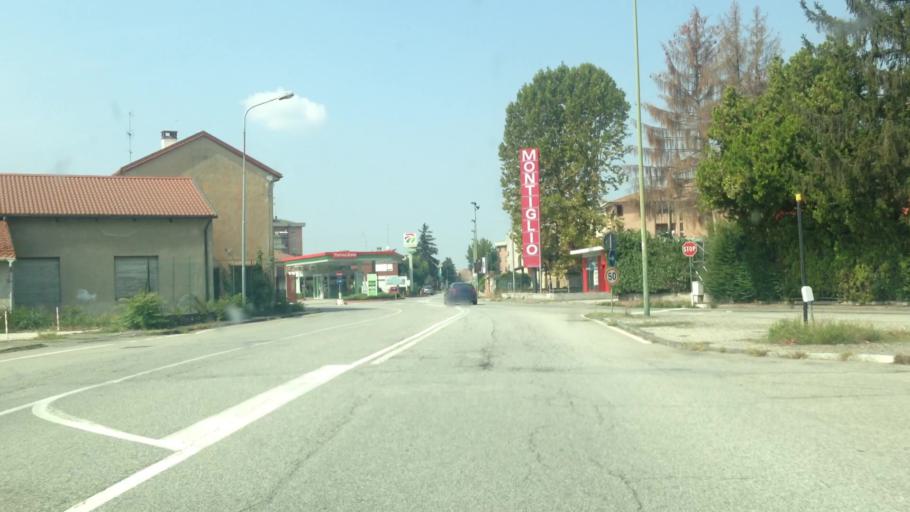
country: IT
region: Piedmont
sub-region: Provincia di Alessandria
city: Casale Monferrato
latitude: 45.1306
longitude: 8.4734
